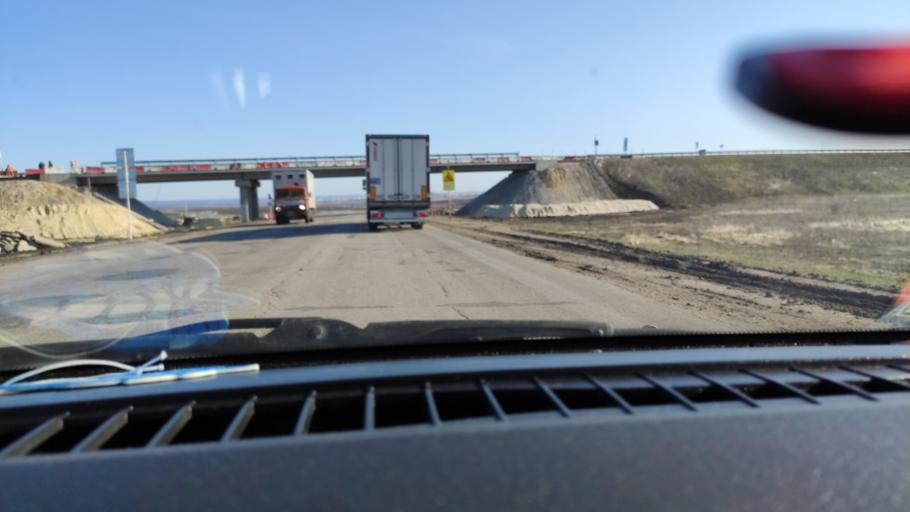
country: RU
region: Samara
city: Syzran'
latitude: 53.0001
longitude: 48.3292
